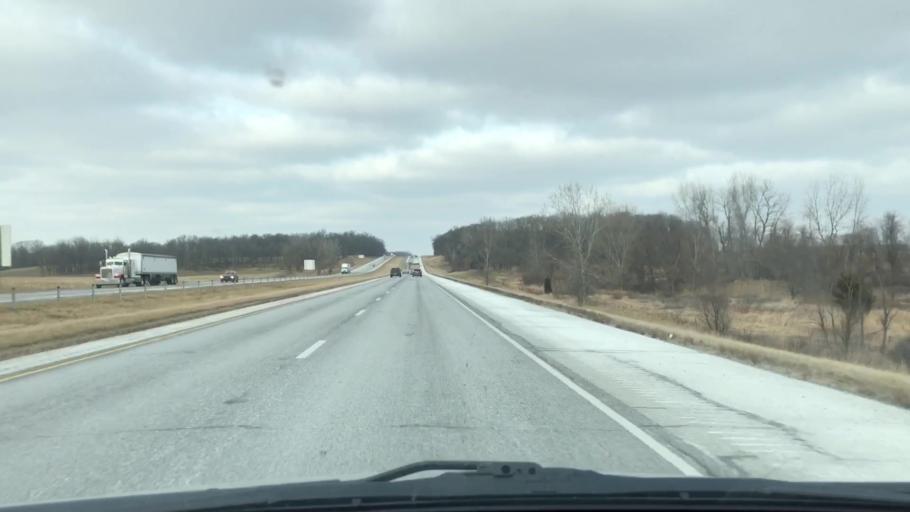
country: US
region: Indiana
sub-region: DeKalb County
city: Waterloo
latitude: 41.4578
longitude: -85.0539
